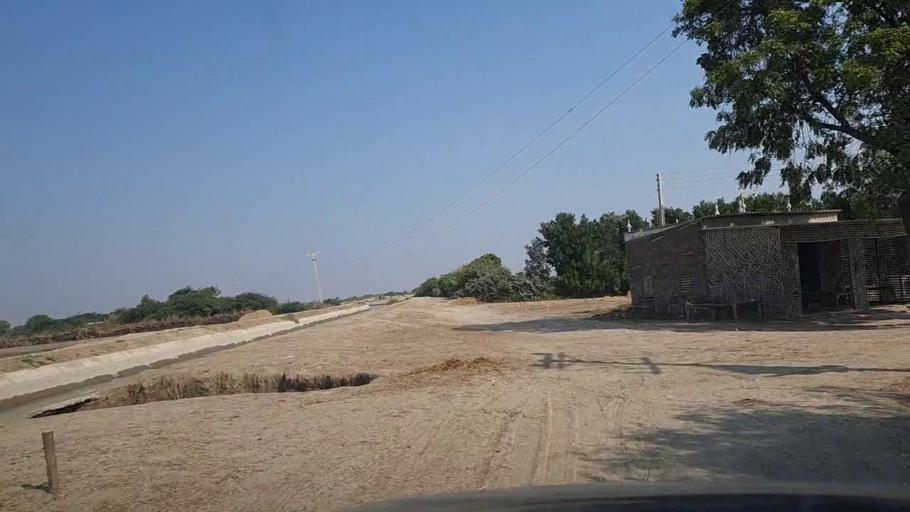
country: PK
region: Sindh
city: Mirpur Sakro
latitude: 24.5235
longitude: 67.8098
